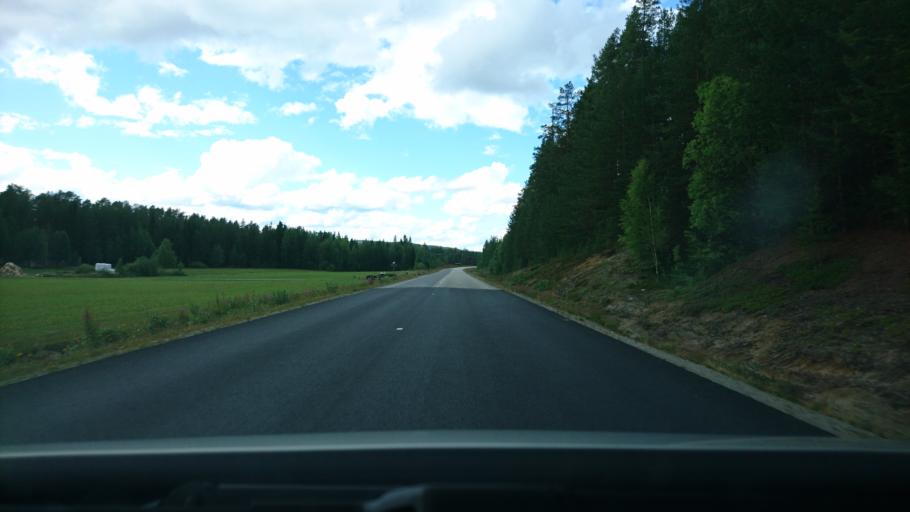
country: SE
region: Vaesterbotten
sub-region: Asele Kommun
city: Asele
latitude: 63.9440
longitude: 17.2814
